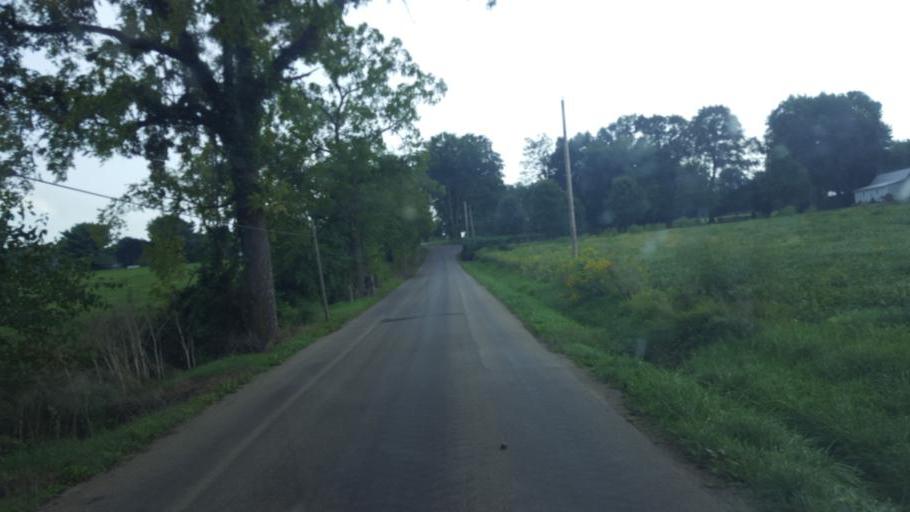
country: US
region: Ohio
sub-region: Knox County
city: Gambier
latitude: 40.3698
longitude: -82.4382
